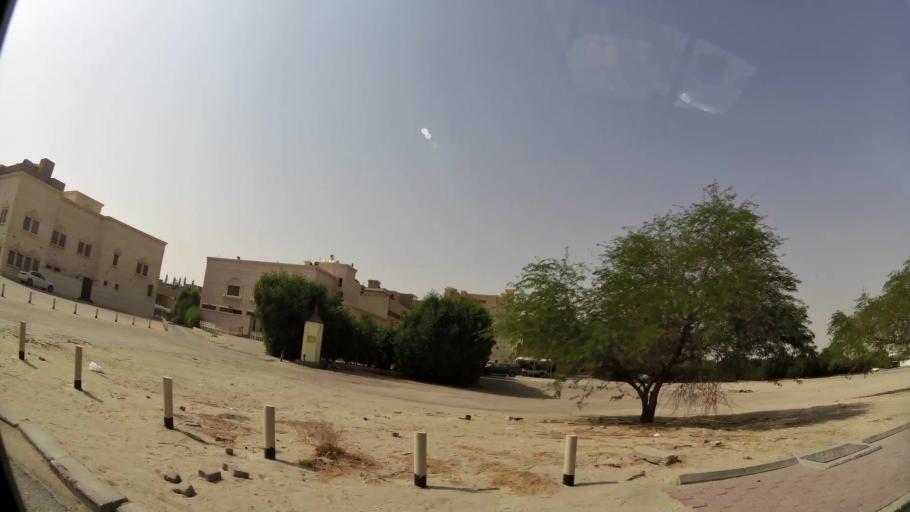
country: KW
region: Muhafazat al Jahra'
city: Al Jahra'
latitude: 29.3236
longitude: 47.6797
